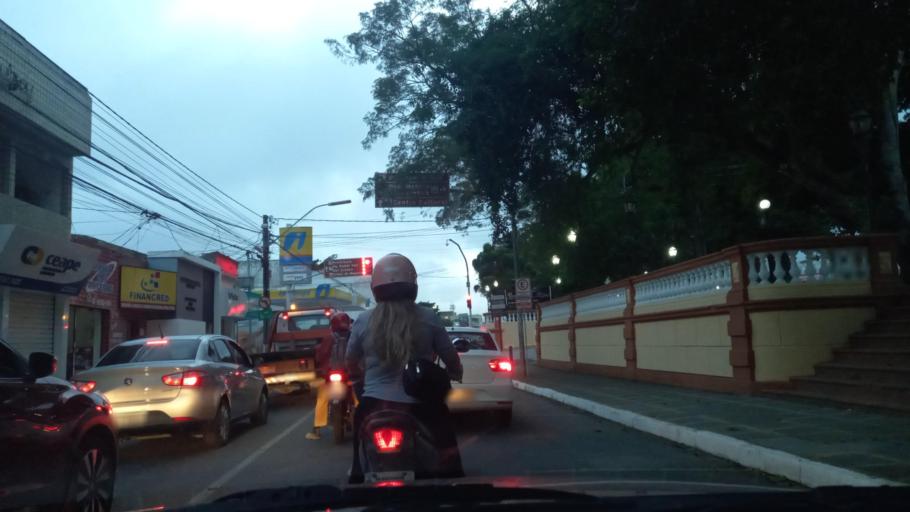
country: BR
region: Pernambuco
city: Garanhuns
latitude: -8.8886
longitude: -36.4919
